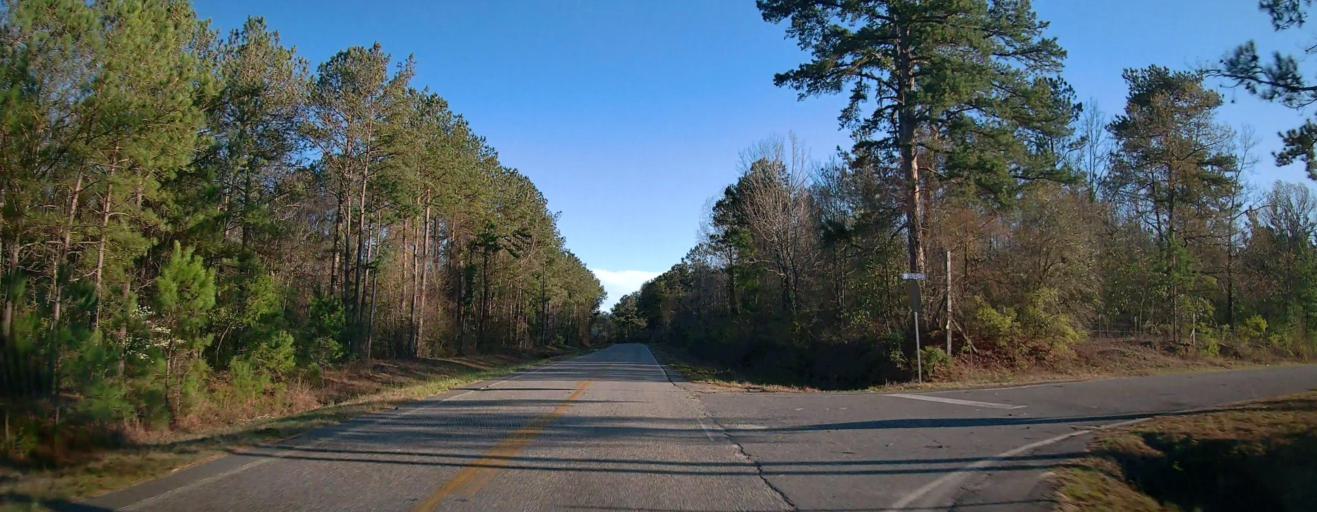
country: US
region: Georgia
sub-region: Wilcox County
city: Abbeville
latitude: 32.0777
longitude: -83.2866
